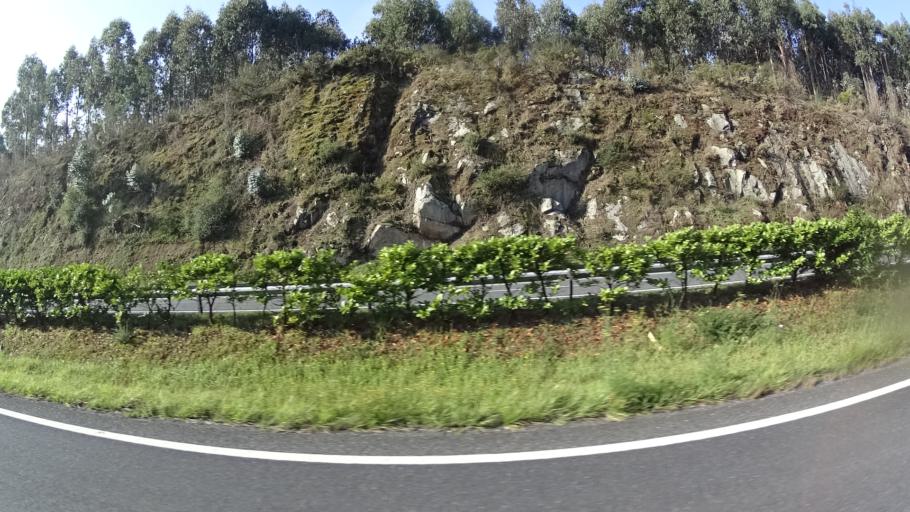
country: ES
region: Galicia
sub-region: Provincia da Coruna
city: Coiros
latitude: 43.2440
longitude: -8.1453
